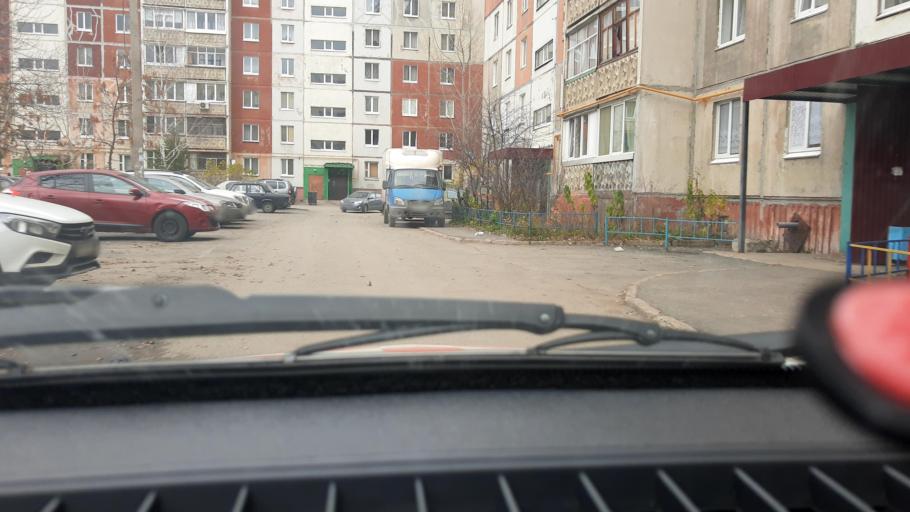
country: RU
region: Bashkortostan
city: Ufa
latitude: 54.7613
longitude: 56.0573
